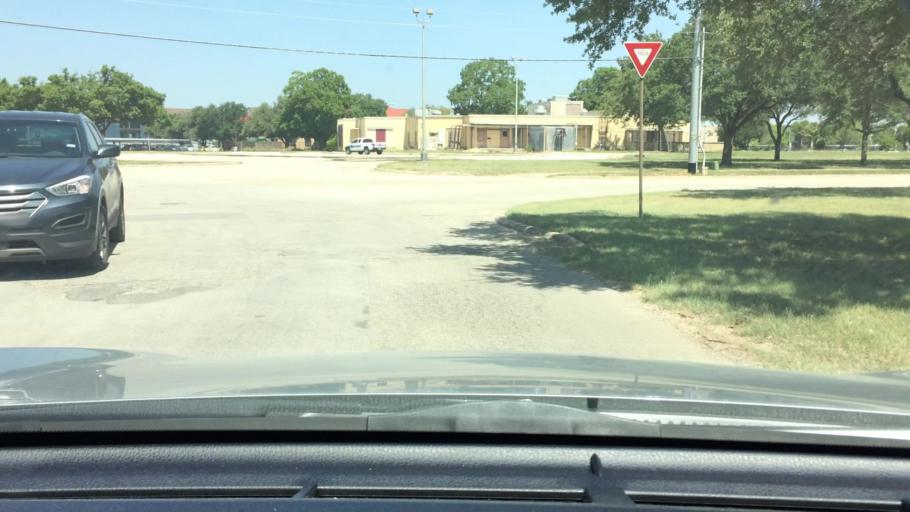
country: US
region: Texas
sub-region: Bexar County
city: San Antonio
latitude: 29.3416
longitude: -98.4456
